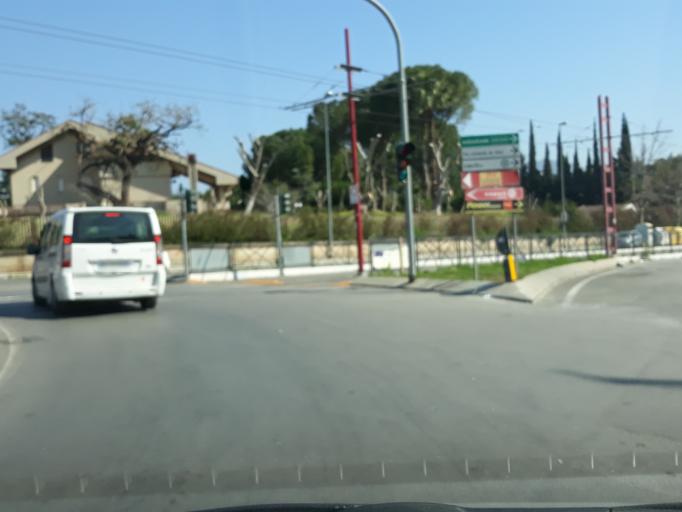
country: IT
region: Sicily
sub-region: Palermo
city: Palermo
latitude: 38.1258
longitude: 13.3029
